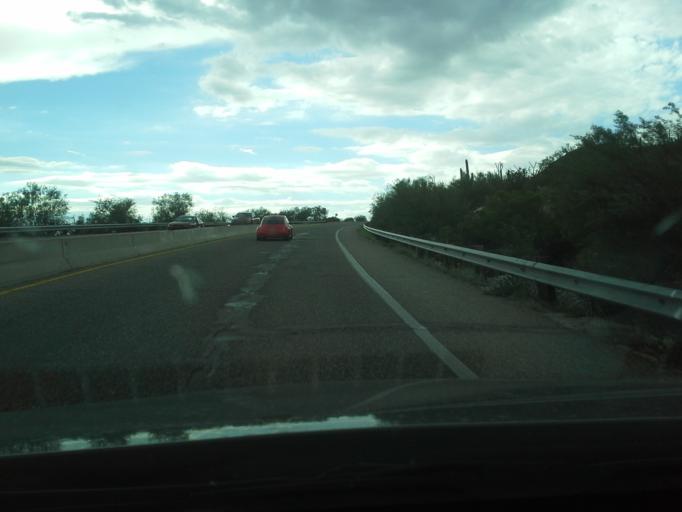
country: US
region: Arizona
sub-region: Pima County
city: South Tucson
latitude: 32.2056
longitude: -110.9936
